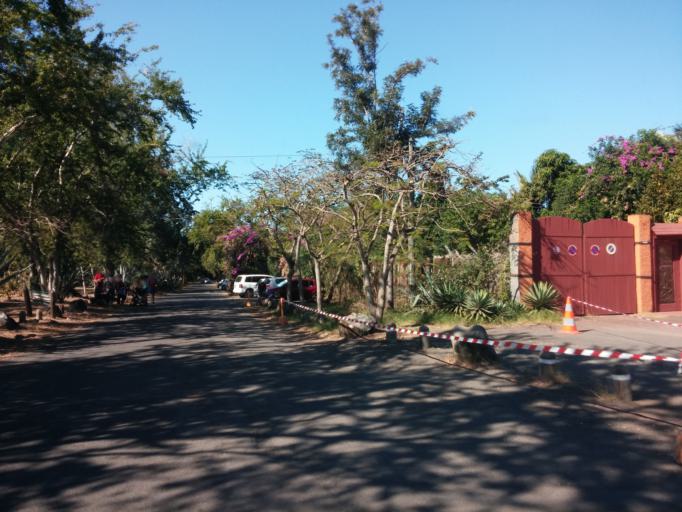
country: RE
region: Reunion
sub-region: Reunion
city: Les Avirons
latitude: -21.2667
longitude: 55.3530
